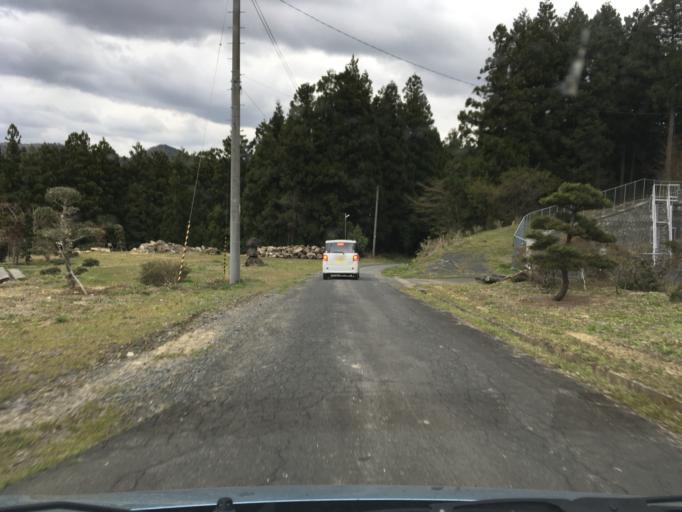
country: JP
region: Iwate
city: Ichinoseki
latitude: 38.9633
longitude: 141.2105
